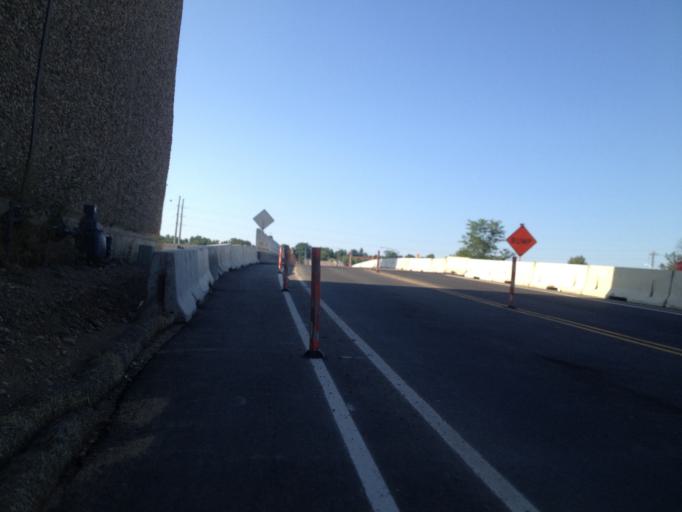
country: US
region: Colorado
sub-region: Boulder County
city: Longmont
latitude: 40.1565
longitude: -105.1070
